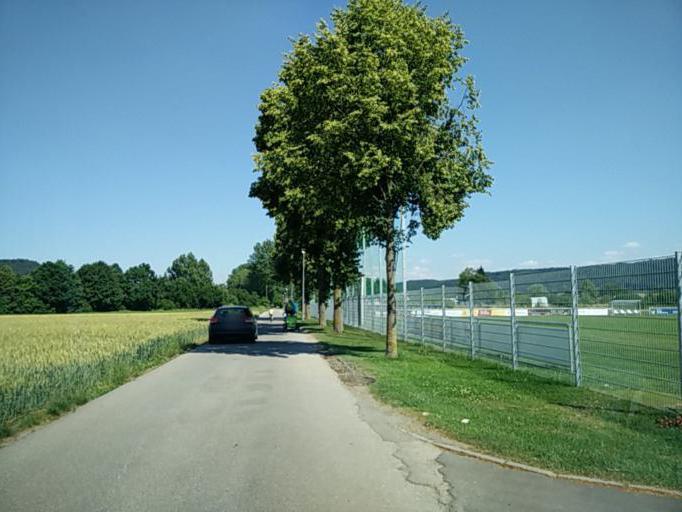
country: DE
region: Baden-Wuerttemberg
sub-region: Tuebingen Region
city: Rottenburg
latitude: 48.5238
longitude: 8.9751
